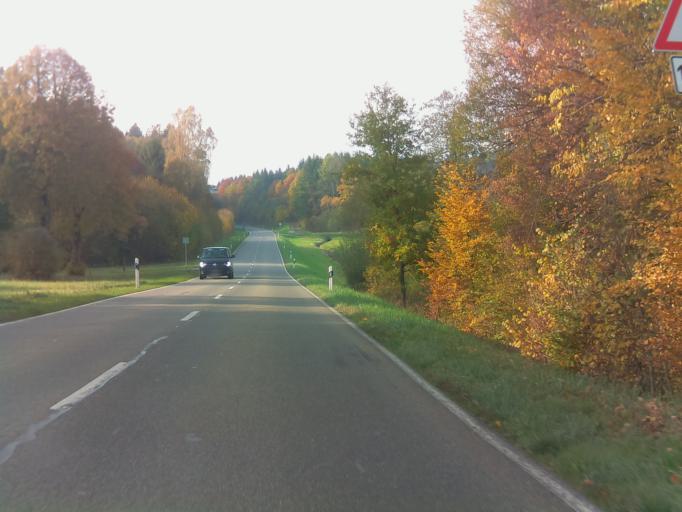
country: DE
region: Baden-Wuerttemberg
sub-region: Karlsruhe Region
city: Seckach
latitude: 49.4068
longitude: 9.3474
